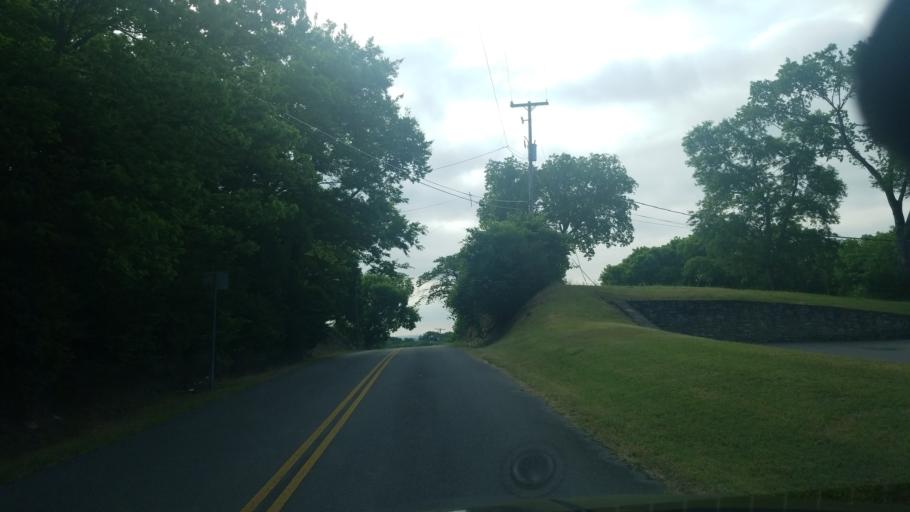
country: US
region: Tennessee
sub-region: Davidson County
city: Nashville
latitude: 36.2365
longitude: -86.7478
